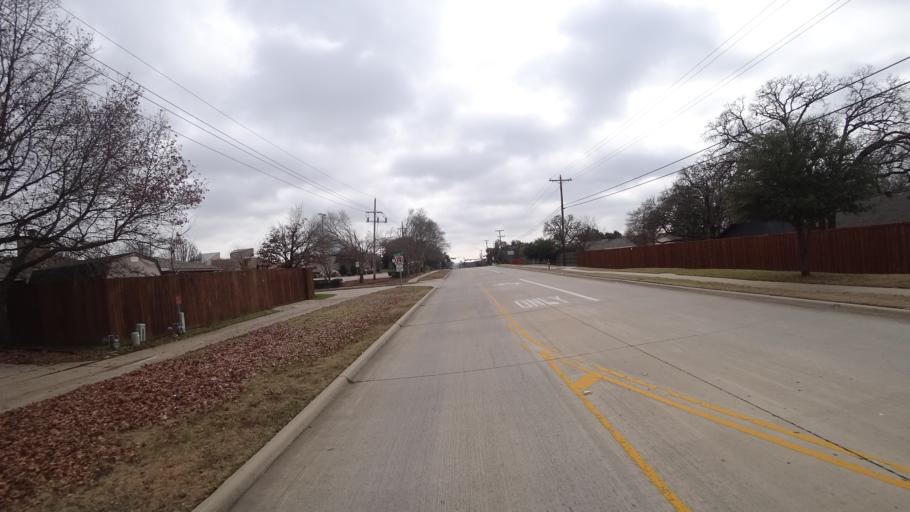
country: US
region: Texas
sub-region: Denton County
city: Highland Village
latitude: 33.0442
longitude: -97.0446
